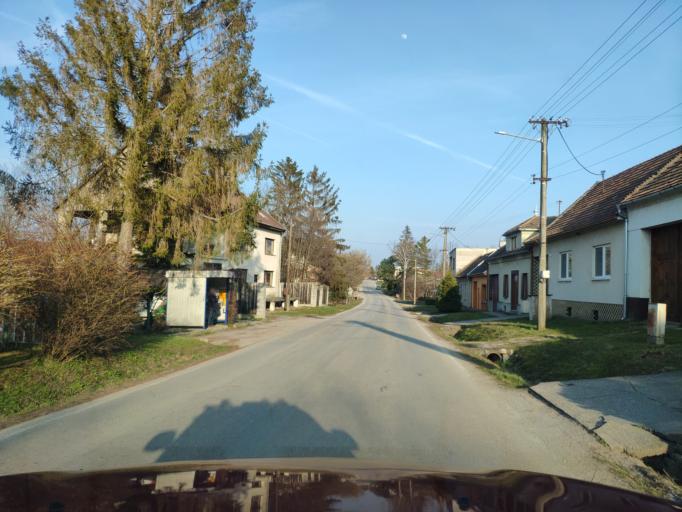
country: SK
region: Bratislavsky
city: Modra
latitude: 48.3344
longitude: 17.3903
